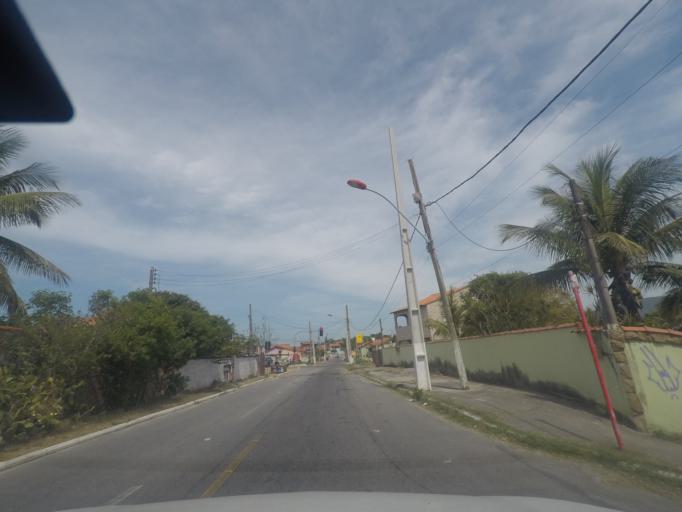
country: BR
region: Rio de Janeiro
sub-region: Marica
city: Marica
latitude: -22.9553
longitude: -42.7463
